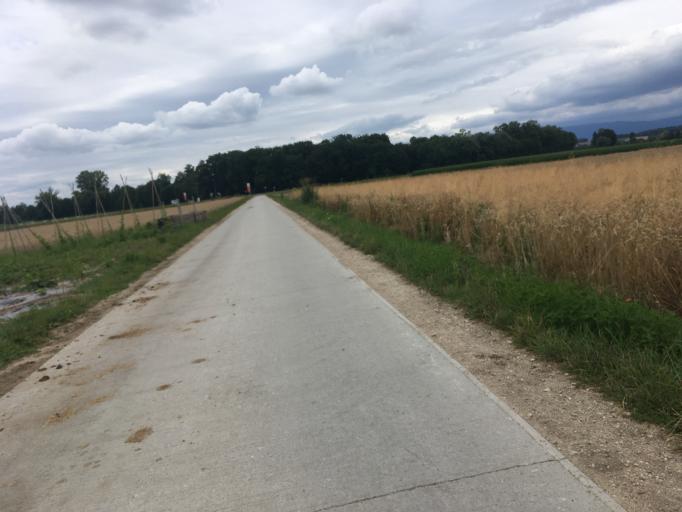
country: CH
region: Vaud
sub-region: Broye-Vully District
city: Avenches
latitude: 46.8871
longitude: 7.0241
